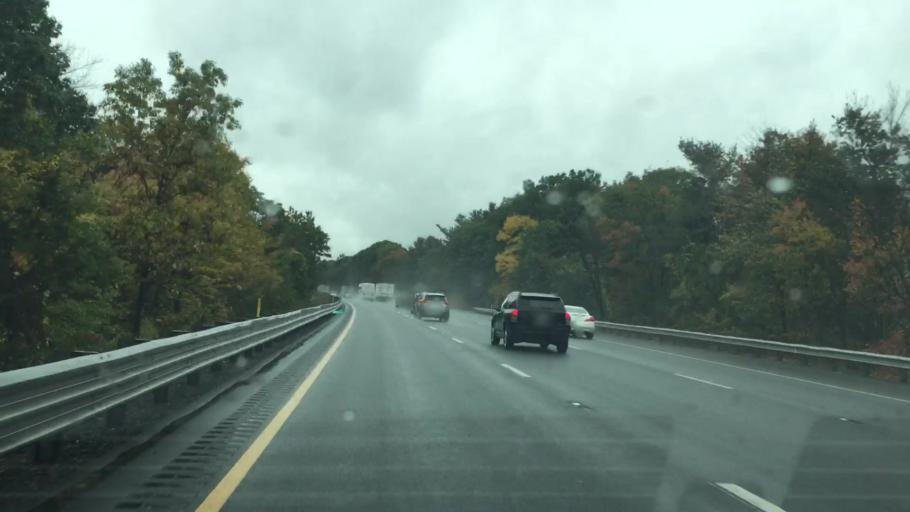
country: US
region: Massachusetts
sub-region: Essex County
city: Haverhill
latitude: 42.8060
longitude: -71.0709
